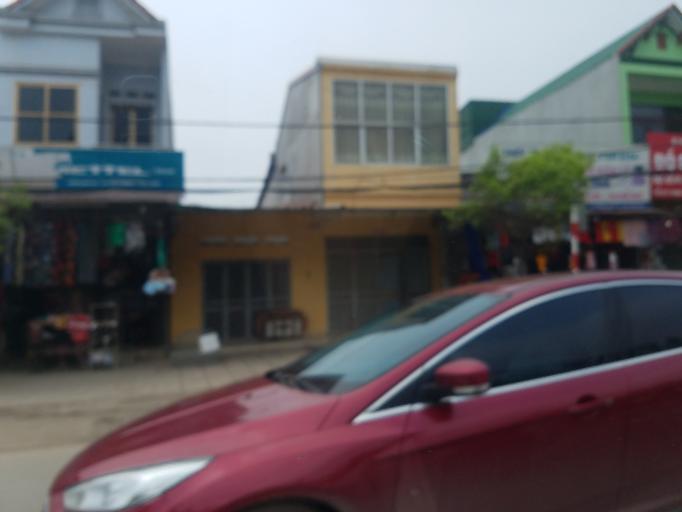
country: VN
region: Thai Nguyen
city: Chua Hang
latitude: 21.6162
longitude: 105.8389
